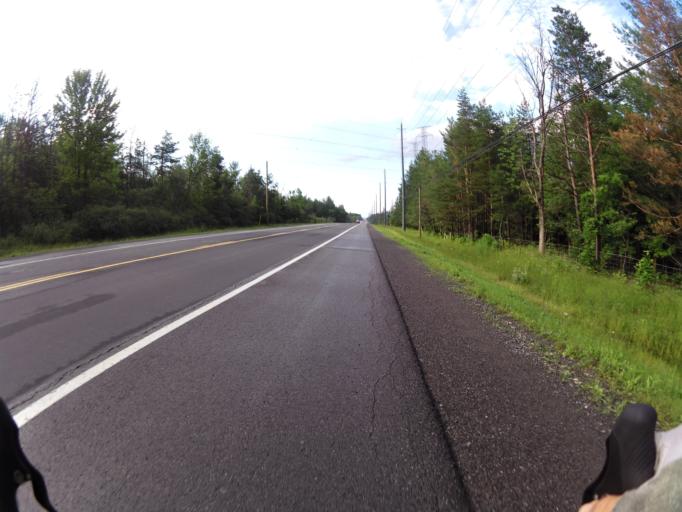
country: CA
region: Ontario
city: Bells Corners
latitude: 45.2930
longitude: -75.8352
